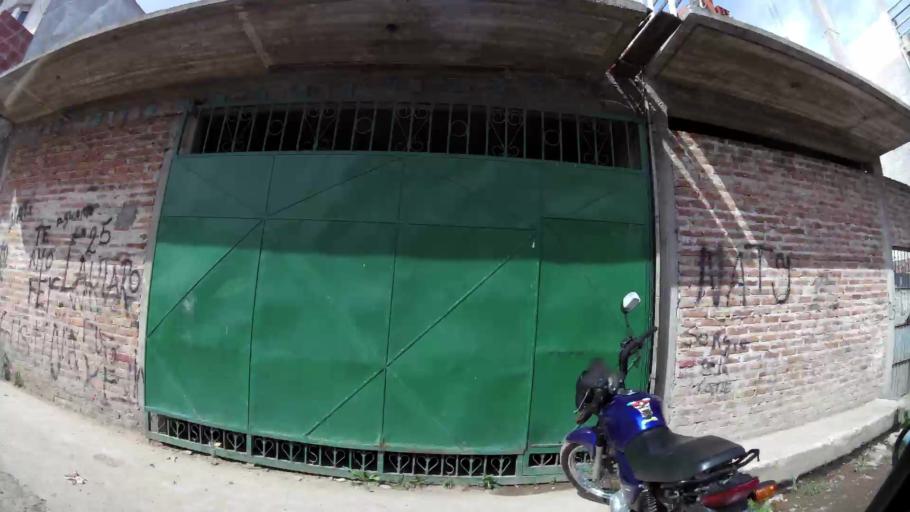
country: AR
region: Buenos Aires
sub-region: Partido de Quilmes
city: Quilmes
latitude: -34.7631
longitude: -58.2499
